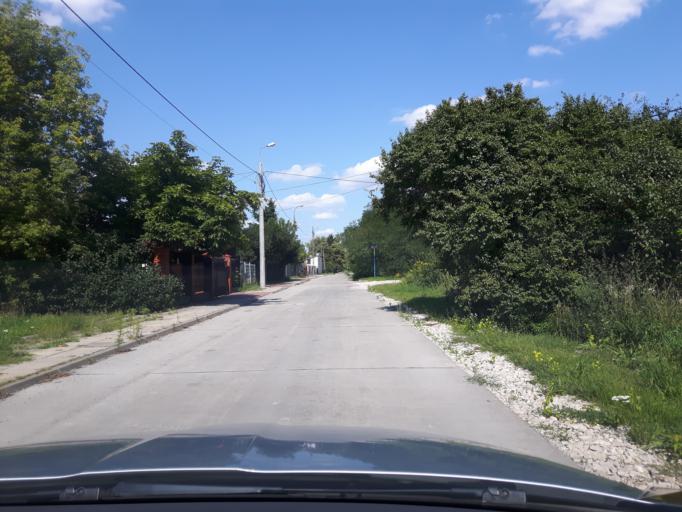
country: PL
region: Masovian Voivodeship
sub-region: Warszawa
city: Praga Poludnie
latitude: 52.2712
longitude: 21.0860
